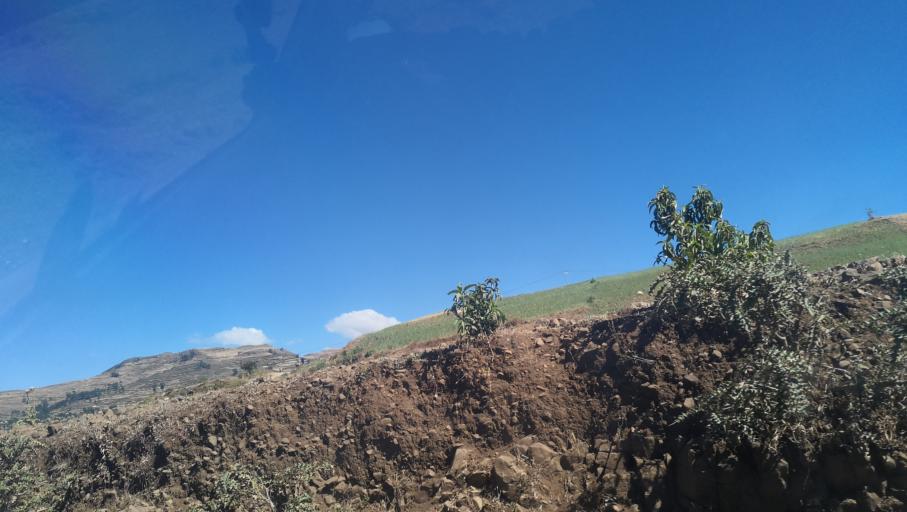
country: ET
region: Amhara
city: Debre Tabor
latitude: 11.5595
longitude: 38.1403
